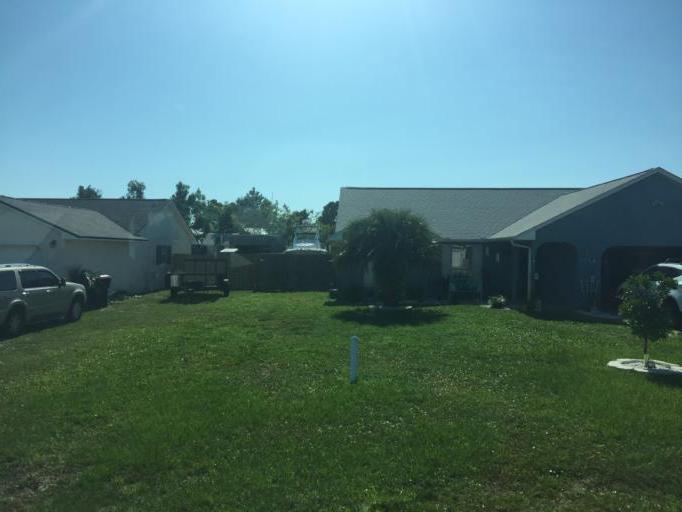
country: US
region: Florida
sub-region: Bay County
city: Panama City Beach
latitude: 30.2035
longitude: -85.8398
